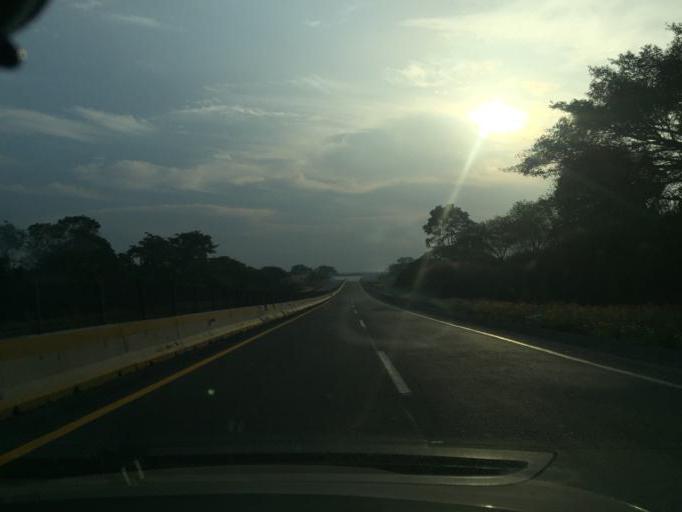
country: MX
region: Veracruz
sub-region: Omealca
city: Mata Tenatito (Casco Hacienda)
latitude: 18.7943
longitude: -96.5788
